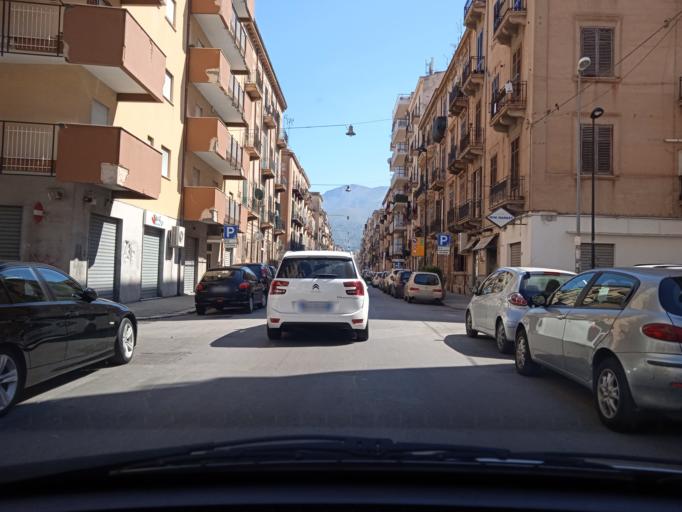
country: IT
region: Sicily
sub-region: Palermo
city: Palermo
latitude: 38.1075
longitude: 13.3655
